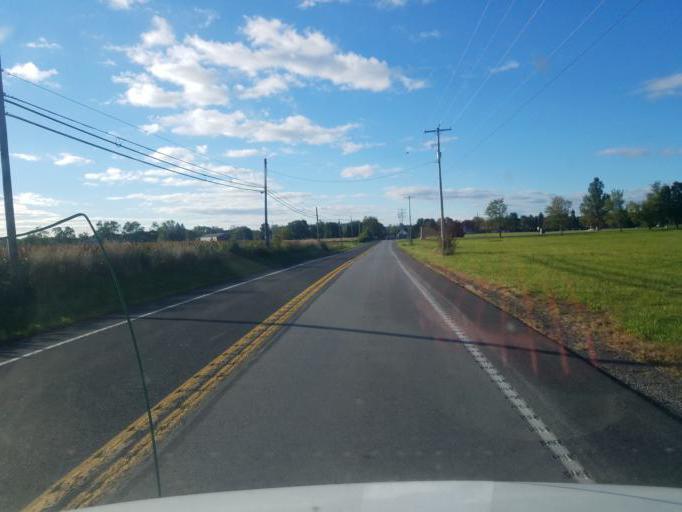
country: US
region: Pennsylvania
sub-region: Adams County
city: Gettysburg
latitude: 39.8447
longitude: -77.2312
